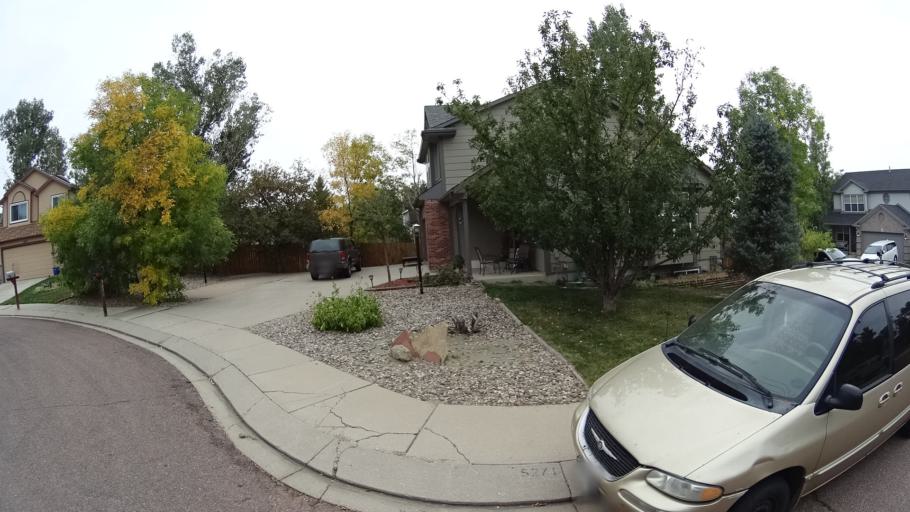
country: US
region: Colorado
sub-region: El Paso County
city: Cimarron Hills
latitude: 38.9089
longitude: -104.7322
